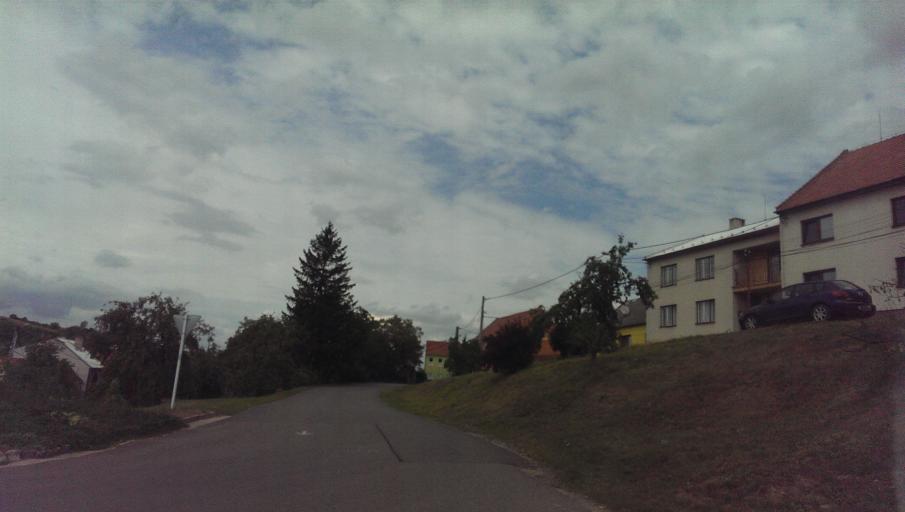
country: CZ
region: South Moravian
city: Velka nad Velickou
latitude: 48.8637
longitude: 17.5909
